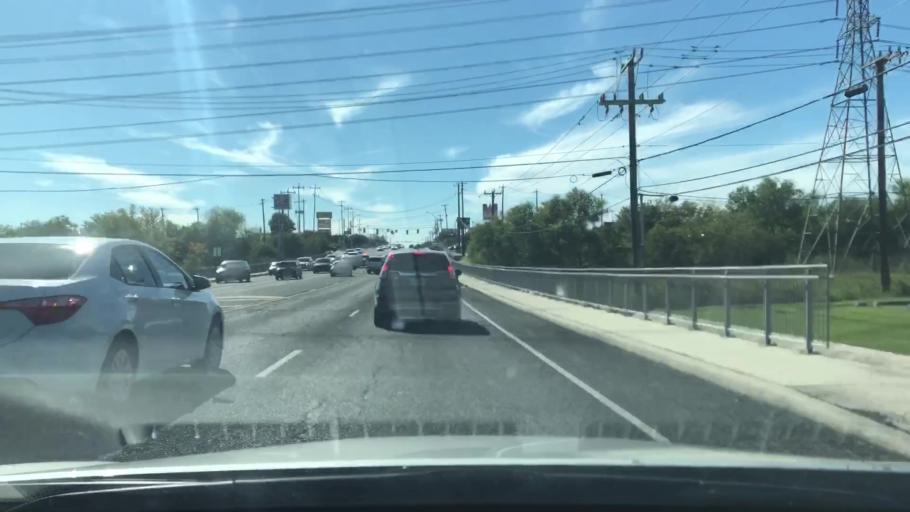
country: US
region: Texas
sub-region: Bexar County
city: Converse
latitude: 29.4928
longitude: -98.3322
